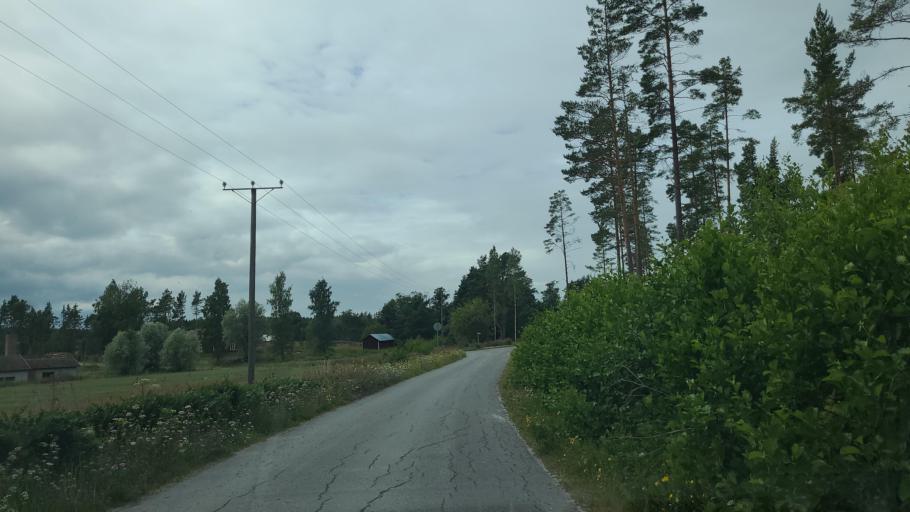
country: FI
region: Varsinais-Suomi
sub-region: Aboland-Turunmaa
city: Dragsfjaerd
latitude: 60.0955
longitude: 22.4225
